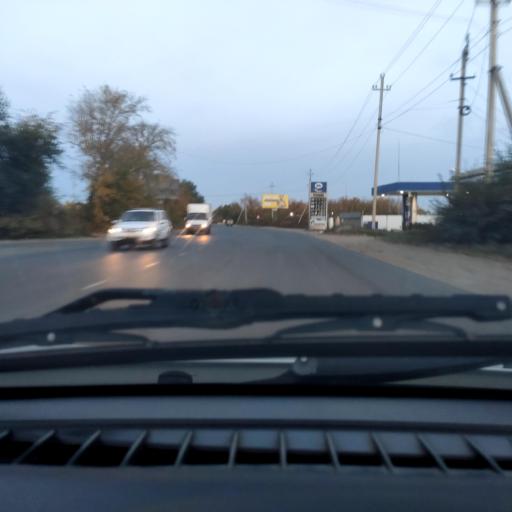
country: RU
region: Samara
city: Tol'yatti
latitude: 53.5291
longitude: 49.4718
